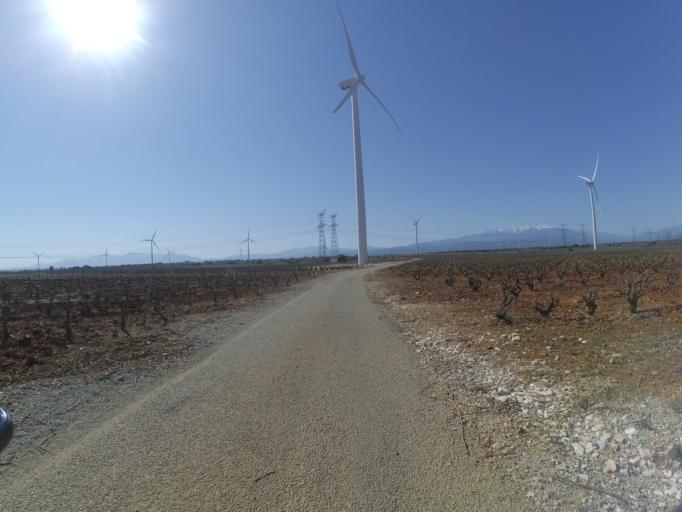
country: FR
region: Languedoc-Roussillon
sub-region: Departement des Pyrenees-Orientales
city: Pezilla-la-Riviere
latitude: 42.7270
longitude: 2.7723
